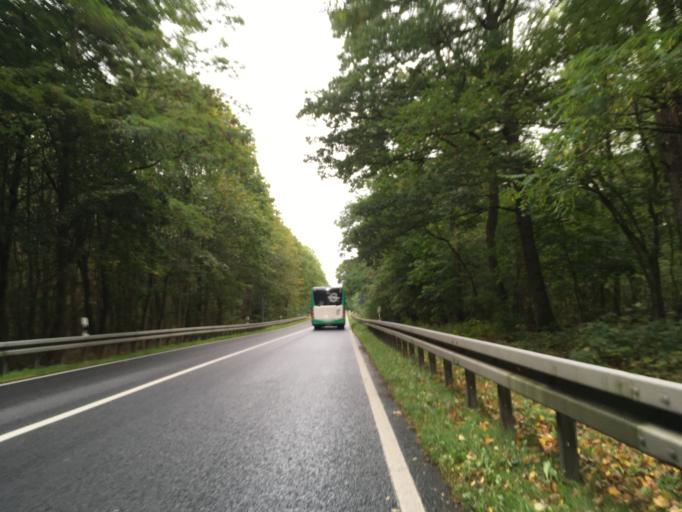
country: DE
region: Brandenburg
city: Werftpfuhl
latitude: 52.6891
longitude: 13.8582
